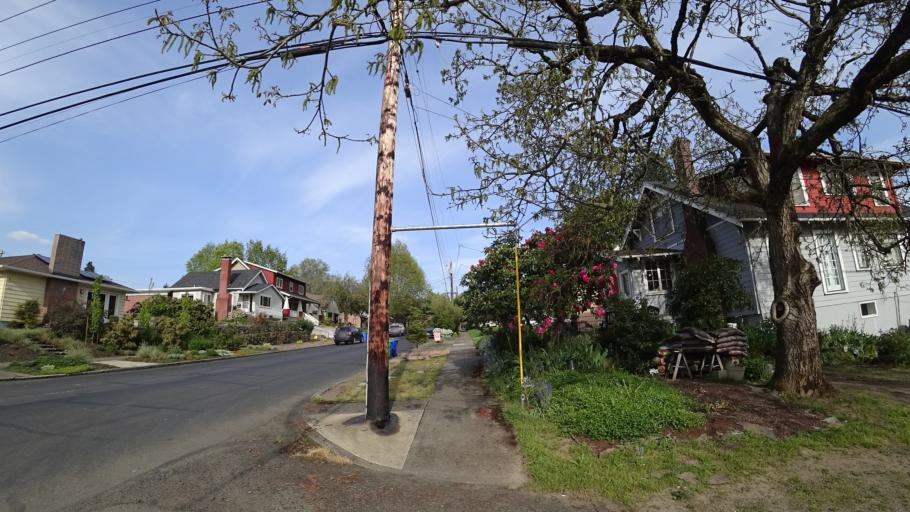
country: US
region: Oregon
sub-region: Clackamas County
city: Milwaukie
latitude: 45.4712
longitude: -122.6195
